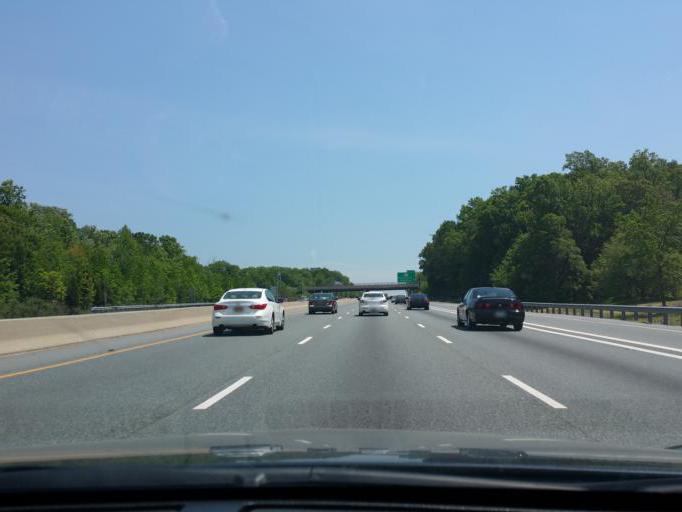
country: US
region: Maryland
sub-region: Harford County
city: Joppatowne
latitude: 39.4547
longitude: -76.3143
